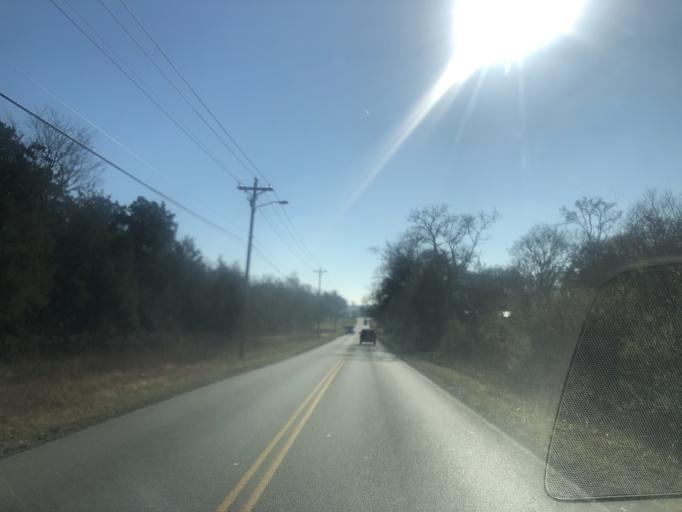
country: US
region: Tennessee
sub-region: Rutherford County
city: La Vergne
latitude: 35.9942
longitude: -86.5552
